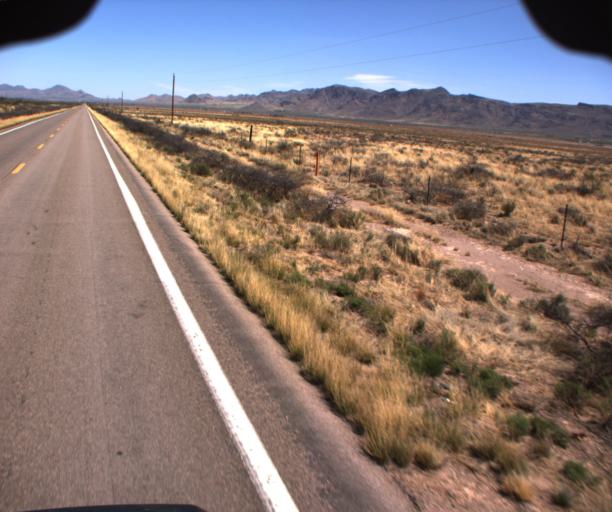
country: US
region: Arizona
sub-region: Cochise County
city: Douglas
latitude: 31.7748
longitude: -109.0742
